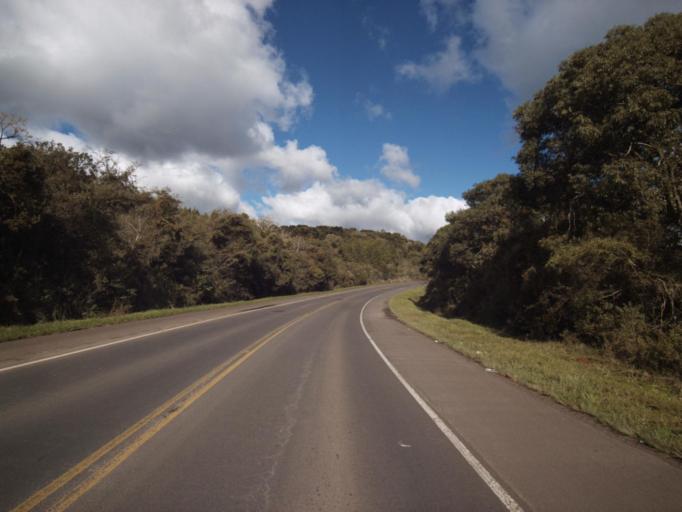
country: BR
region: Santa Catarina
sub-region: Joacaba
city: Joacaba
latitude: -27.0310
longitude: -51.7224
